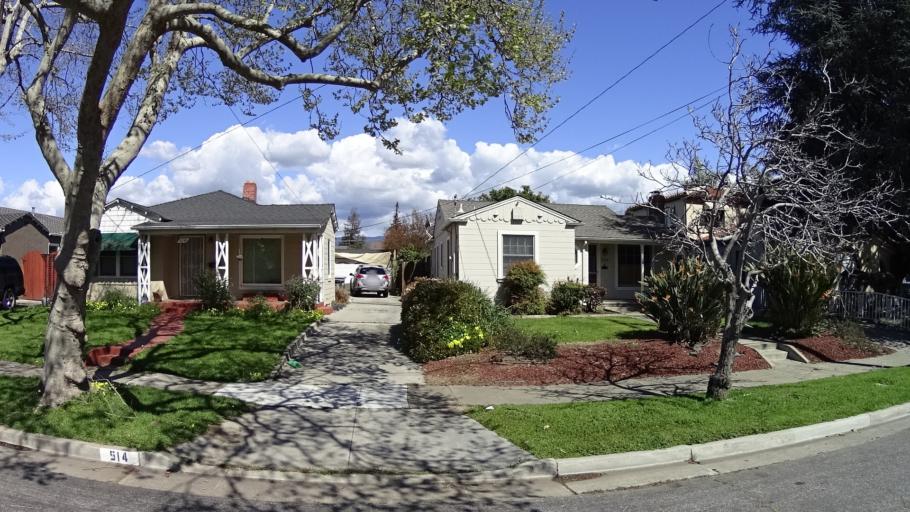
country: US
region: California
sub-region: Santa Clara County
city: San Jose
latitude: 37.3536
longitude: -121.8792
